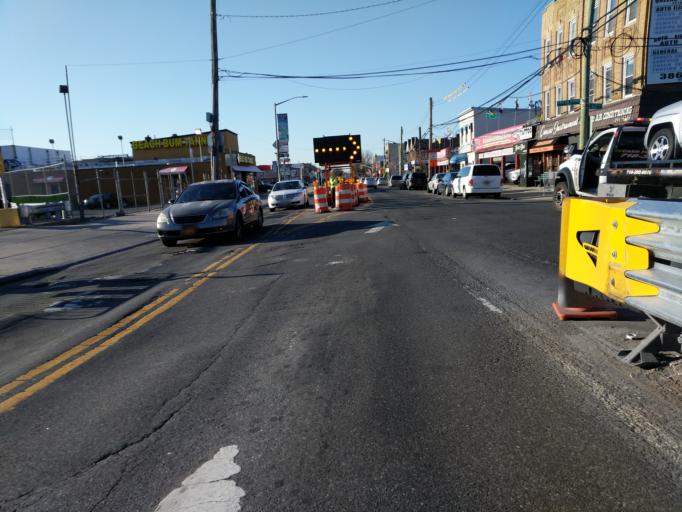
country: US
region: New York
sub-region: Kings County
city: East New York
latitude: 40.7130
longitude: -73.9008
